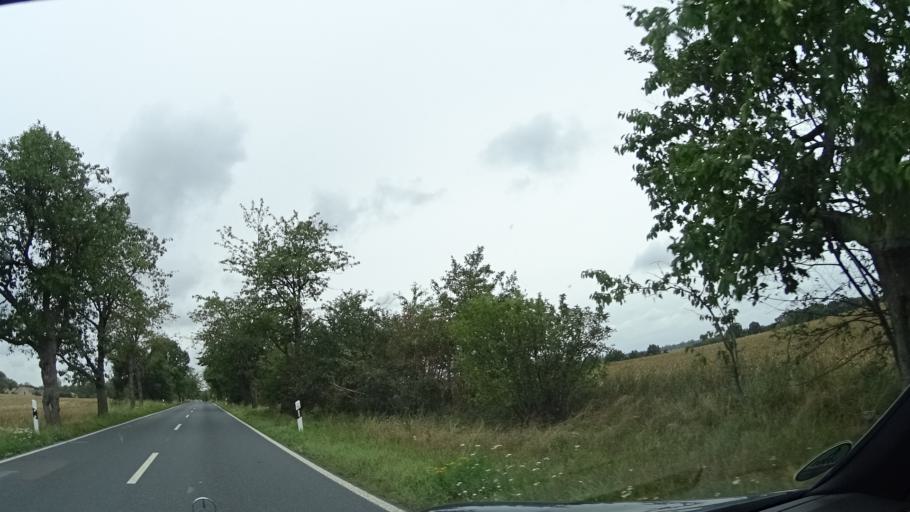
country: DE
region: Brandenburg
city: Dabergotz
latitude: 52.9433
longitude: 12.7151
